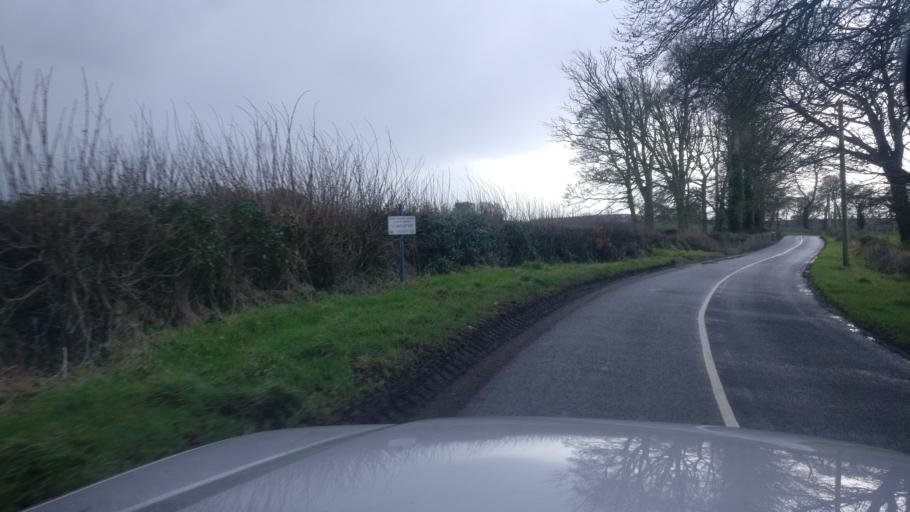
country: IE
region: Munster
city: Nenagh Bridge
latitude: 52.9724
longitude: -8.0896
